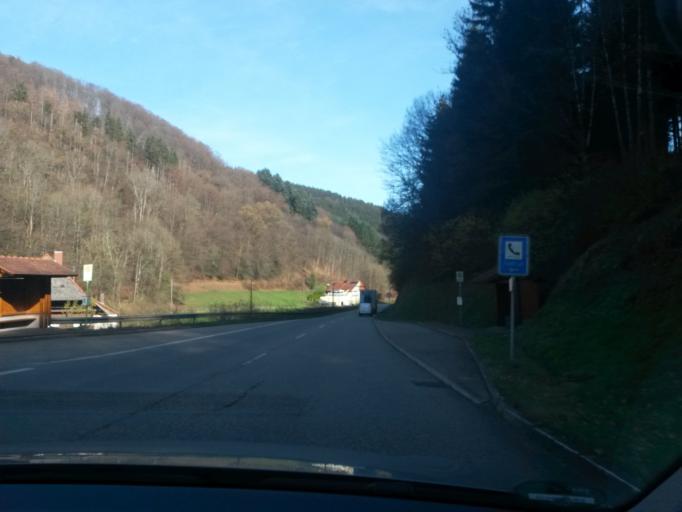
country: DE
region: Baden-Wuerttemberg
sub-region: Freiburg Region
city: Muhlenbach
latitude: 48.2330
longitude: 8.1015
